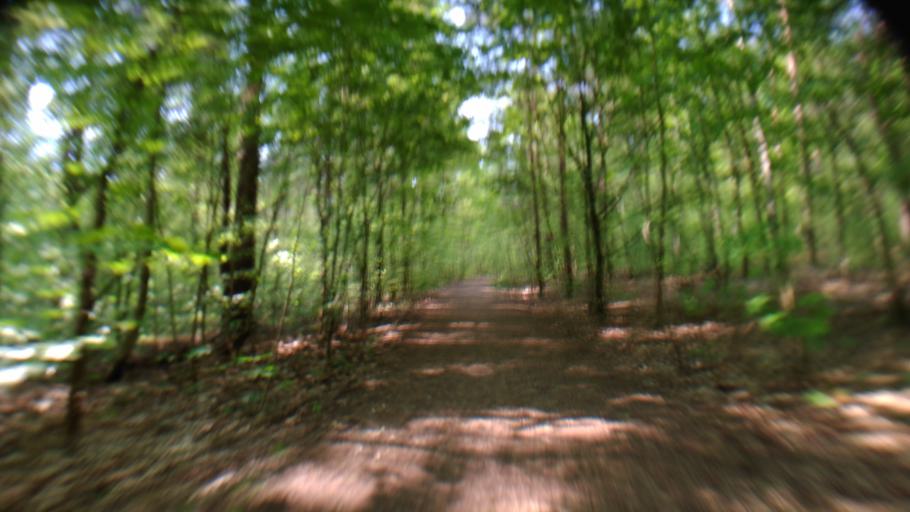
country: DE
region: Saxony
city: Albertstadt
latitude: 51.0785
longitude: 13.7883
